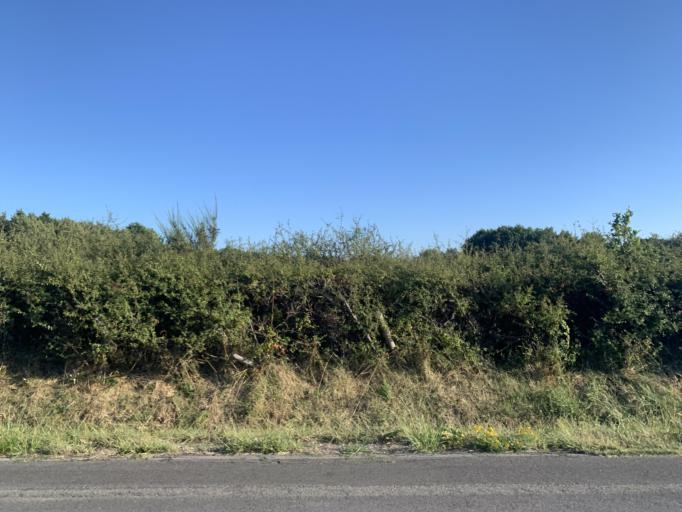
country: FR
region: Pays de la Loire
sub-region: Departement de la Loire-Atlantique
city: Pornichet
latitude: 47.2593
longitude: -2.2866
